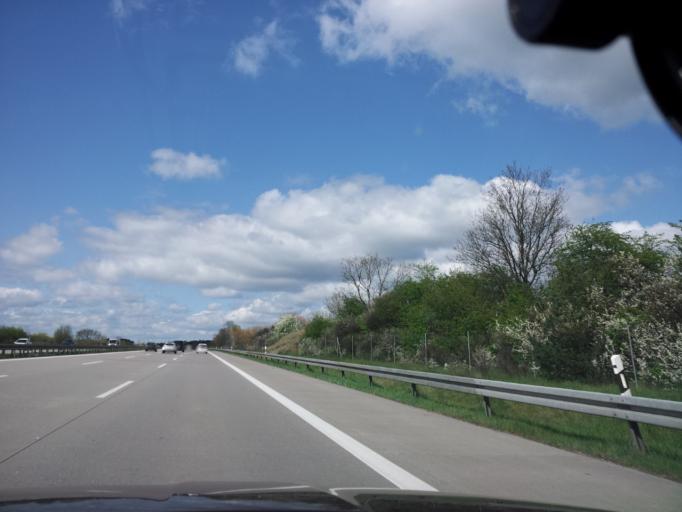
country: DE
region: Berlin
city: Hellersdorf
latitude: 52.5733
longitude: 13.6440
